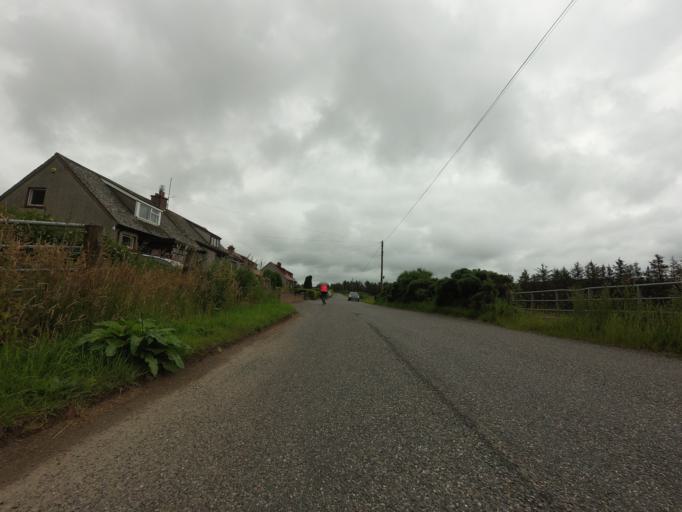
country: GB
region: Scotland
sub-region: Aberdeenshire
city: Turriff
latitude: 57.5341
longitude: -2.3767
